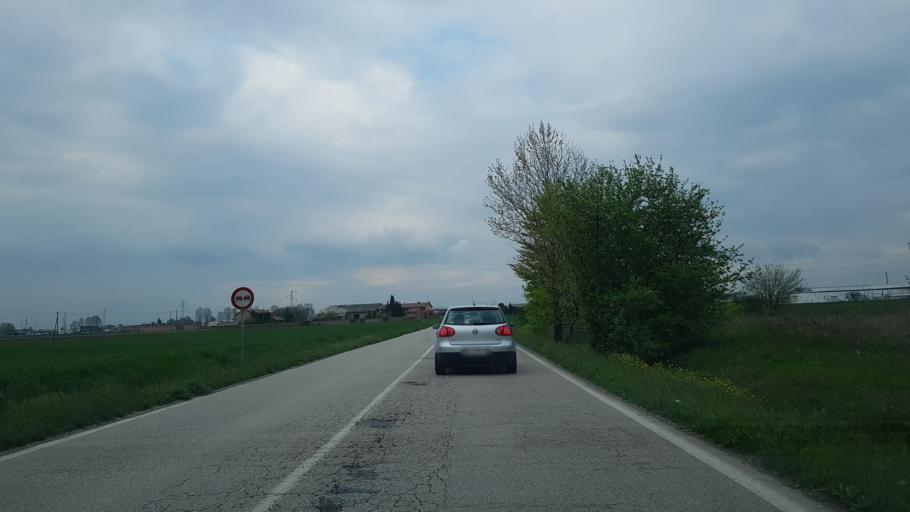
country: IT
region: Veneto
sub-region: Provincia di Verona
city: Legnago
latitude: 45.1786
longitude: 11.2510
